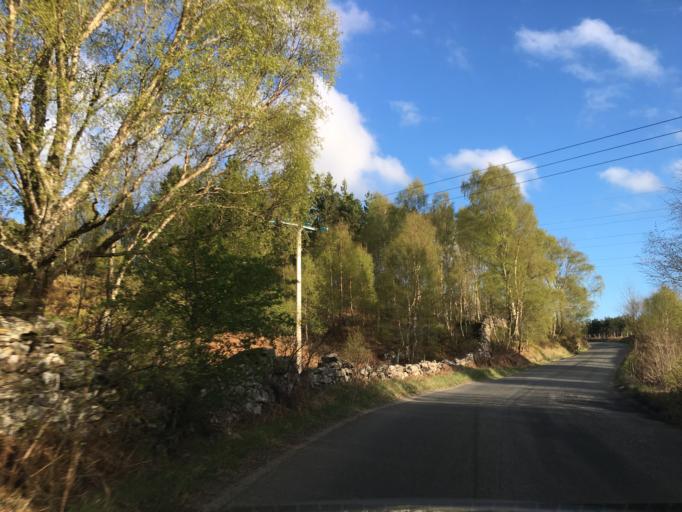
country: GB
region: Scotland
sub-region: Perth and Kinross
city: Aberfeldy
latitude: 56.7032
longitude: -4.0003
